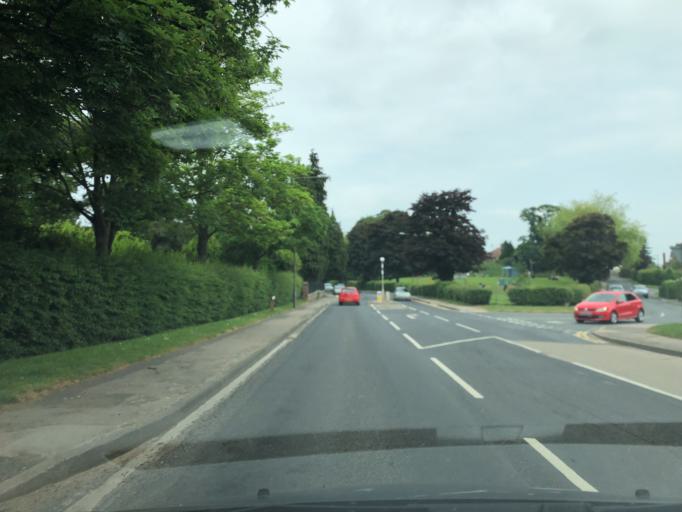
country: GB
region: England
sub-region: North Yorkshire
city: Boroughbridge
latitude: 54.0897
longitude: -1.3973
